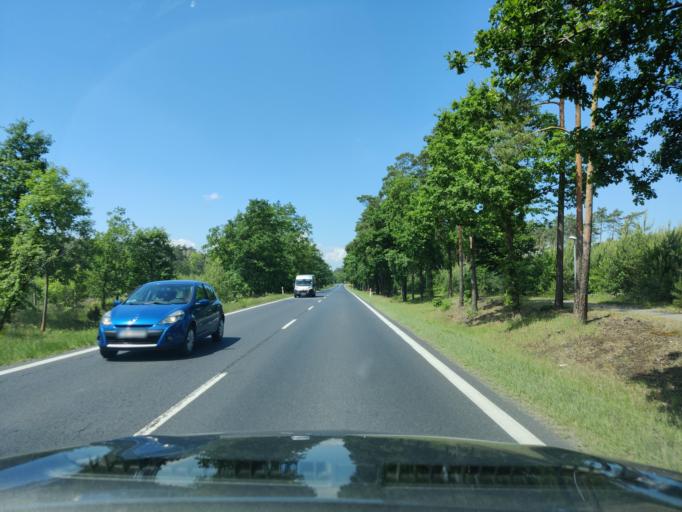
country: PL
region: Greater Poland Voivodeship
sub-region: Powiat grodziski
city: Rakoniewice
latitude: 52.1346
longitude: 16.2401
